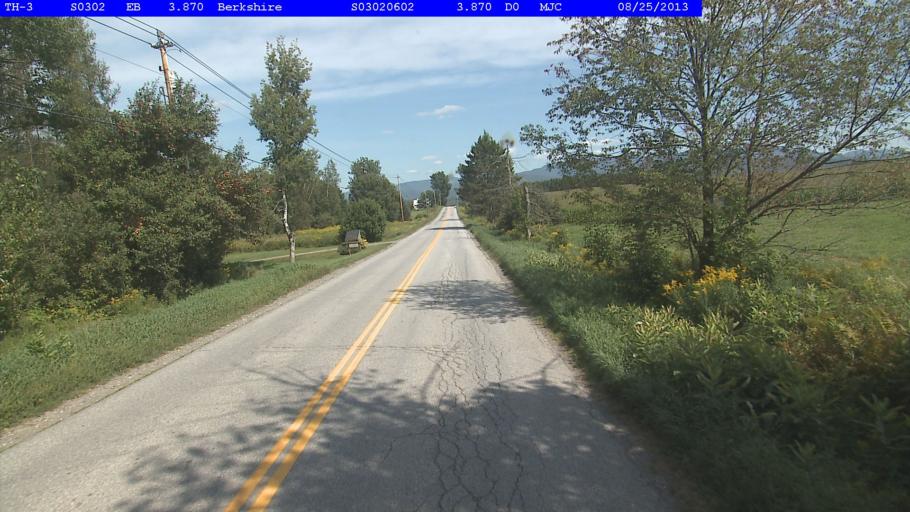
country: US
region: Vermont
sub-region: Franklin County
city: Richford
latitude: 44.9790
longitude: -72.7433
